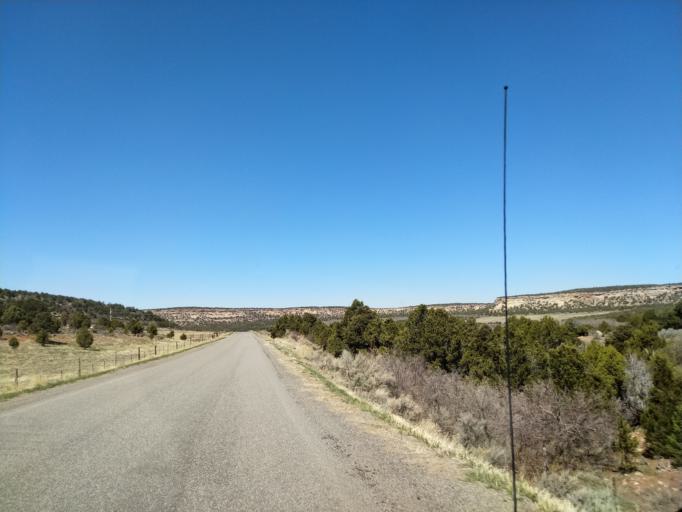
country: US
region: Colorado
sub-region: Mesa County
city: Loma
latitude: 38.9563
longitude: -109.0002
